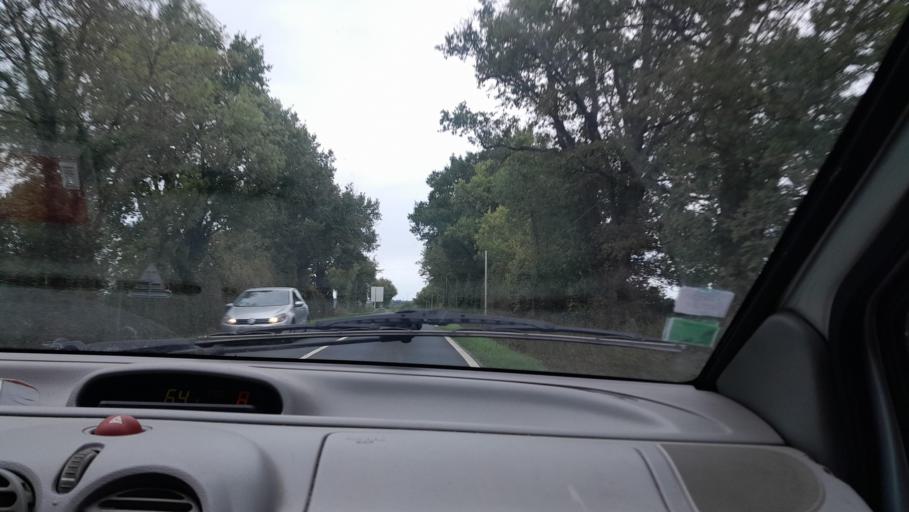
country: FR
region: Pays de la Loire
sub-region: Departement de la Loire-Atlantique
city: Saint-Mars-la-Jaille
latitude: 47.4721
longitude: -1.1749
